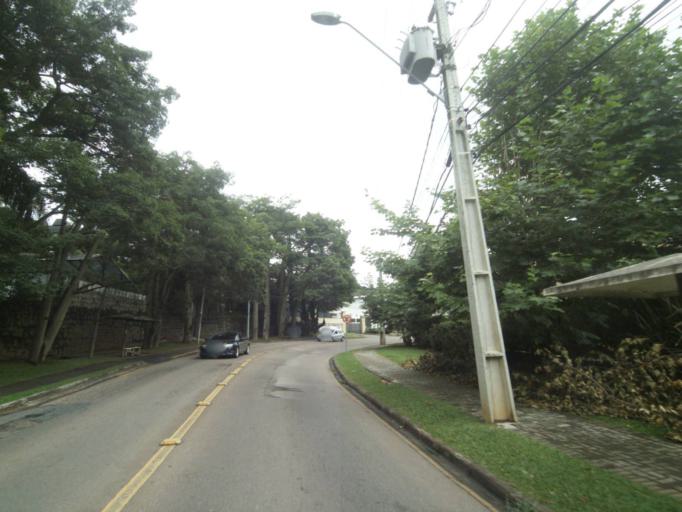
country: BR
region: Parana
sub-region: Curitiba
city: Curitiba
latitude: -25.4496
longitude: -49.3269
